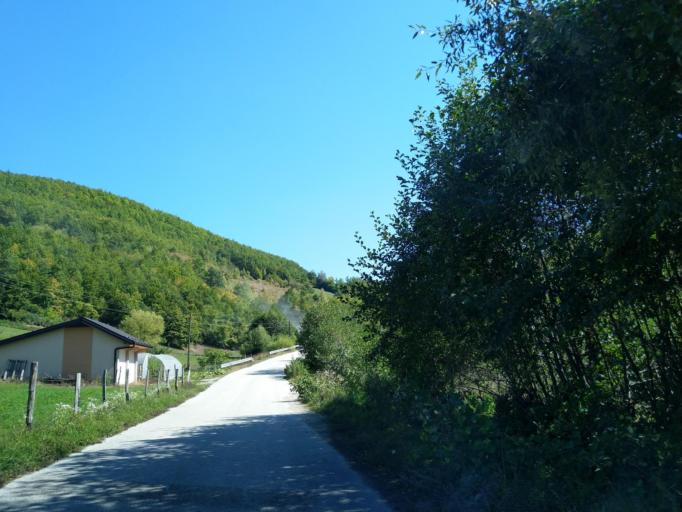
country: RS
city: Sokolovica
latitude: 43.2605
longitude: 20.2982
